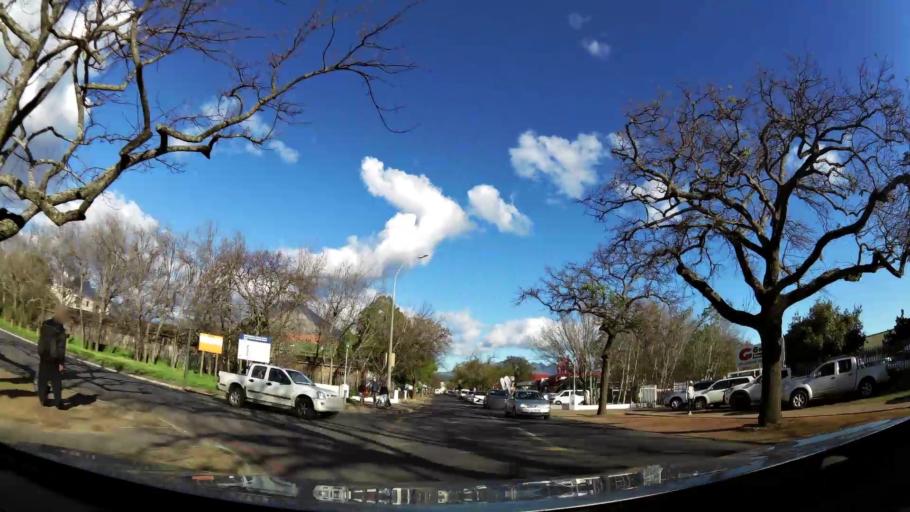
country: ZA
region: Western Cape
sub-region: Cape Winelands District Municipality
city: Stellenbosch
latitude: -33.9272
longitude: 18.8566
